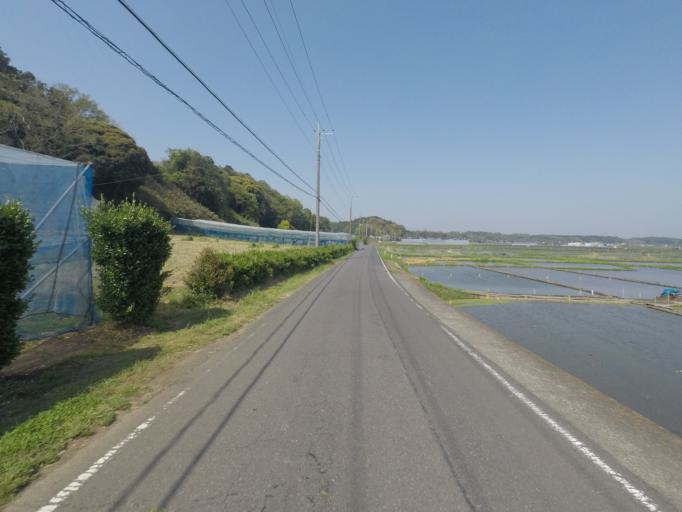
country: JP
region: Ibaraki
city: Ami
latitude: 36.0664
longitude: 140.2954
